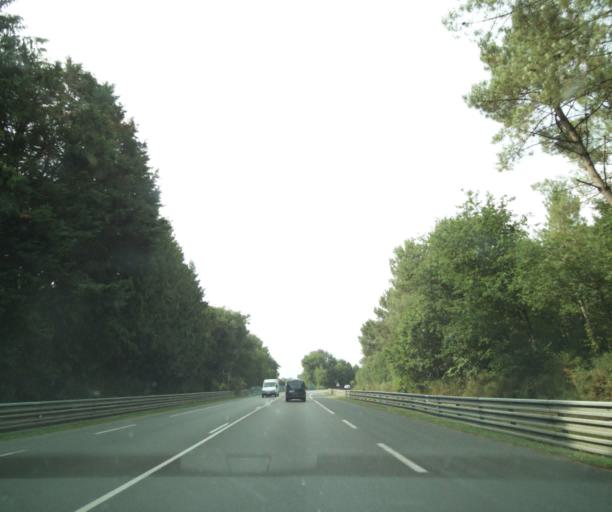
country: FR
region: Pays de la Loire
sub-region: Departement de la Sarthe
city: Mulsanne
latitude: 47.9381
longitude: 0.2367
